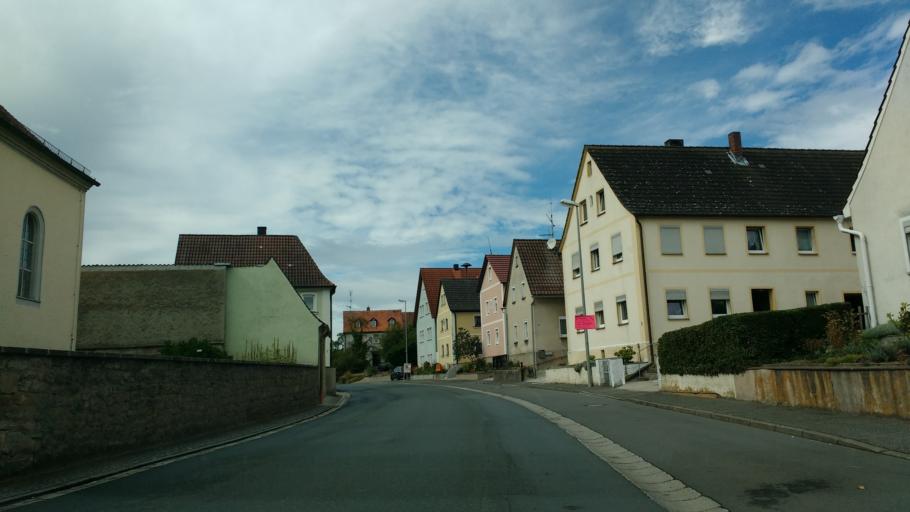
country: DE
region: Bavaria
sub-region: Upper Franconia
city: Schlusselfeld
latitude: 49.7604
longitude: 10.6086
